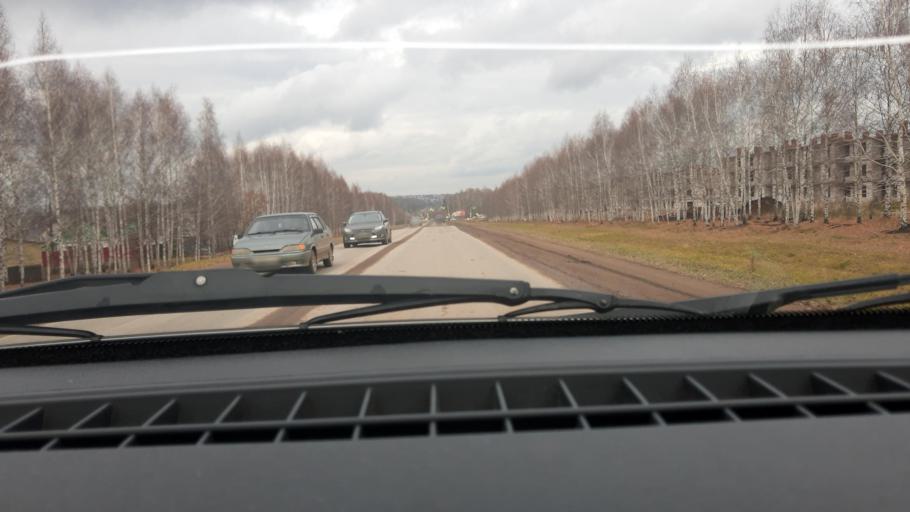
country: RU
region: Bashkortostan
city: Iglino
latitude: 54.8252
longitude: 56.4229
